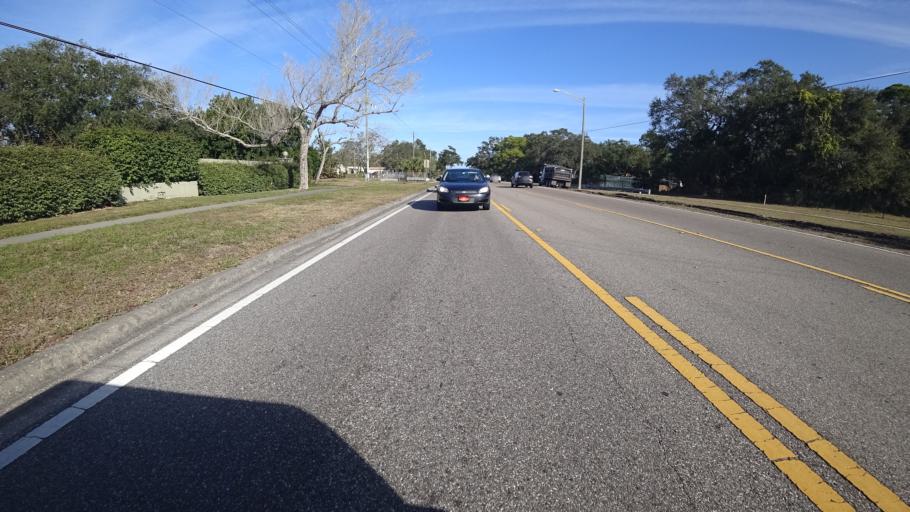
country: US
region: Florida
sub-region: Manatee County
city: West Bradenton
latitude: 27.4771
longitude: -82.6205
